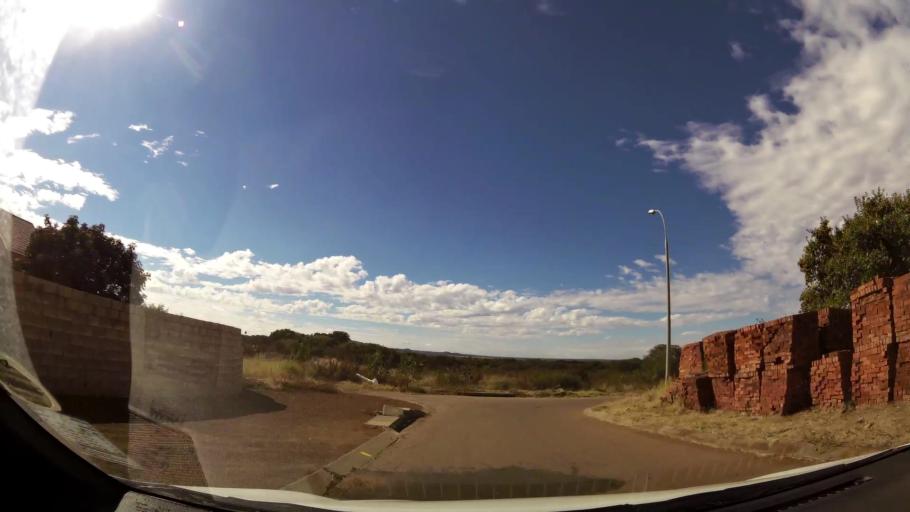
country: ZA
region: Limpopo
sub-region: Waterberg District Municipality
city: Bela-Bela
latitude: -24.8709
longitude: 28.2912
